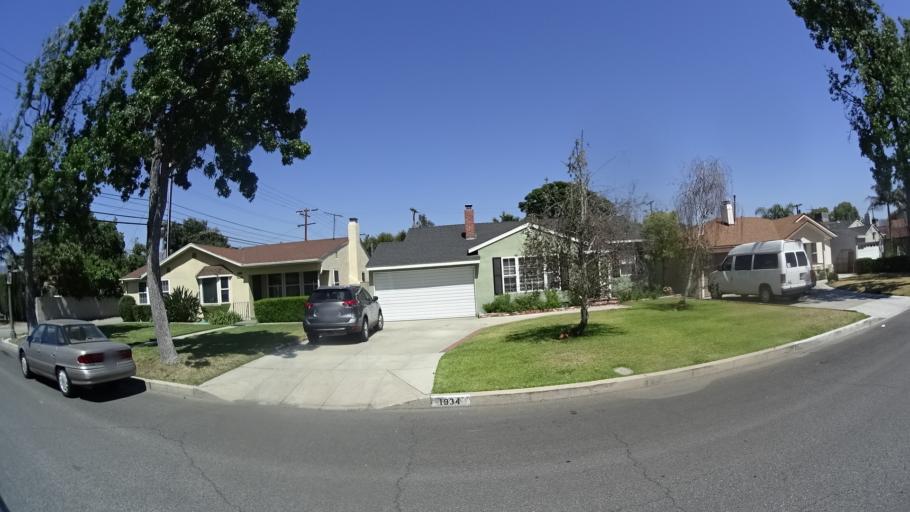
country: US
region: California
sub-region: Los Angeles County
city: North Hollywood
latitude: 34.1843
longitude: -118.3524
